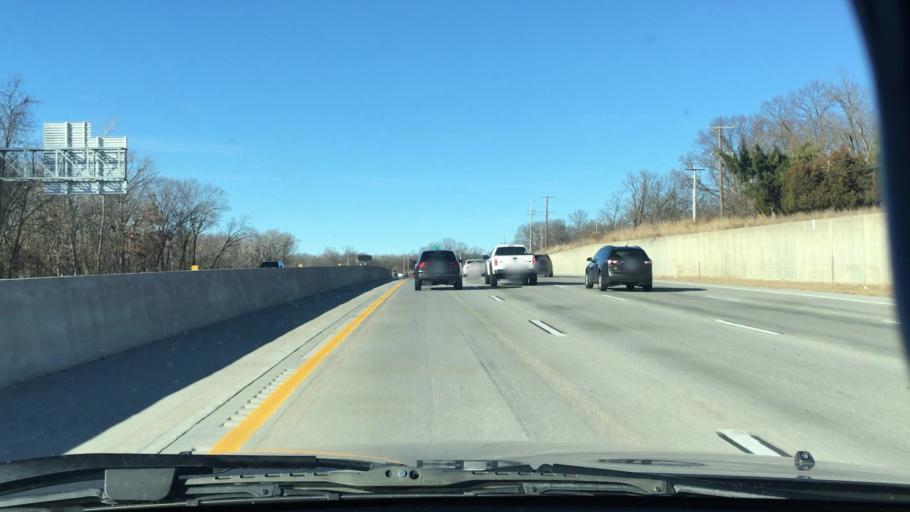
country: US
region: Missouri
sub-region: Saint Charles County
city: Weldon Spring
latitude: 38.6937
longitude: -90.6653
